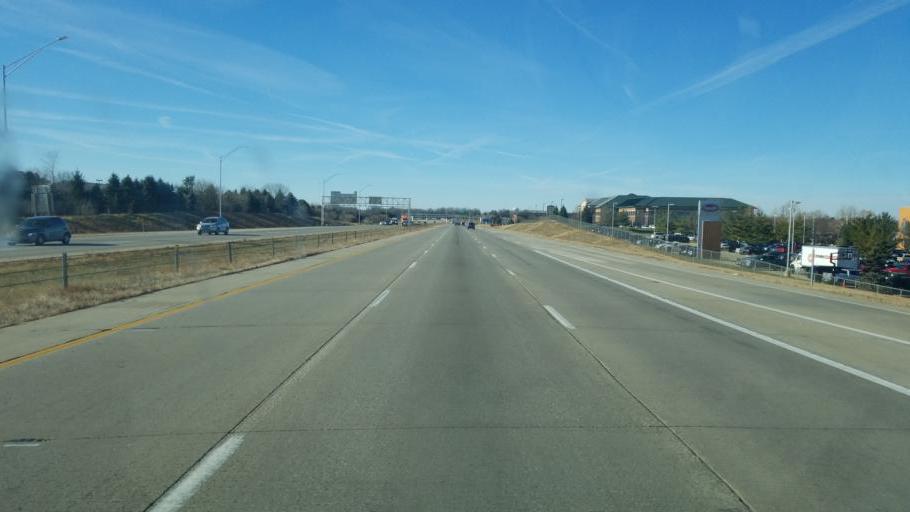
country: US
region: Iowa
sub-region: Polk County
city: Clive
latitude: 41.5923
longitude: -93.7947
